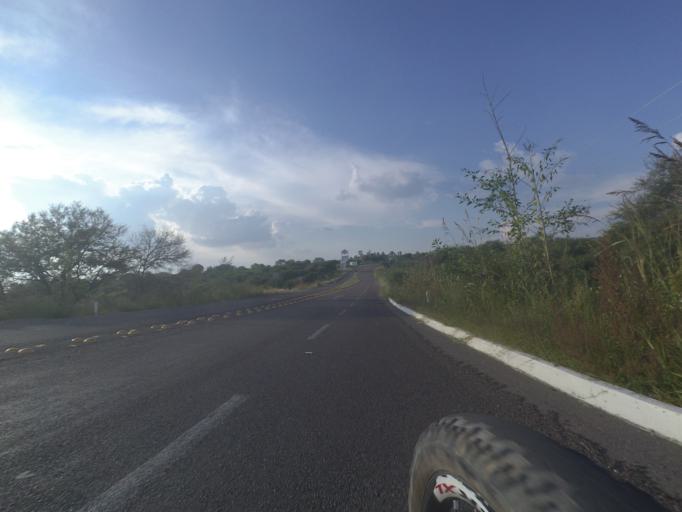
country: MX
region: Aguascalientes
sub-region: Aguascalientes
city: Penuelas (El Cienegal)
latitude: 21.7681
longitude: -102.3580
